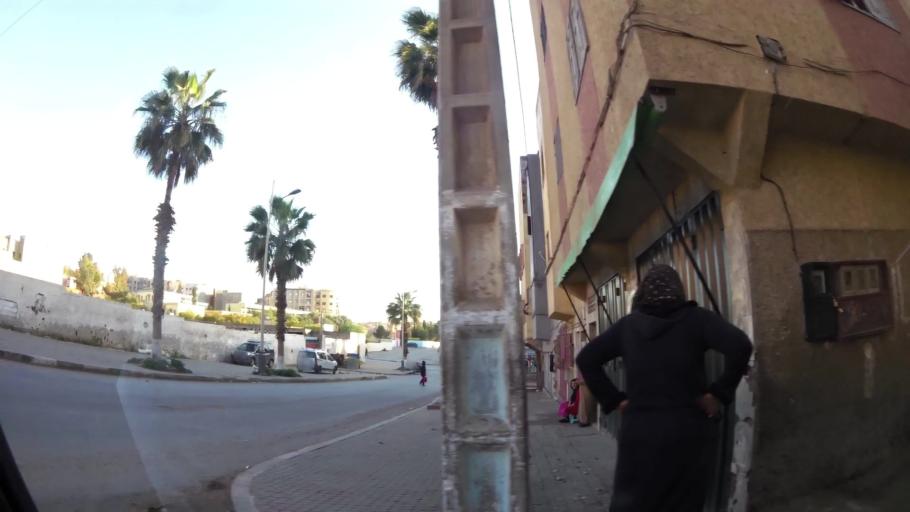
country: MA
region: Chaouia-Ouardigha
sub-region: Settat Province
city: Settat
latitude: 32.9960
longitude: -7.6050
